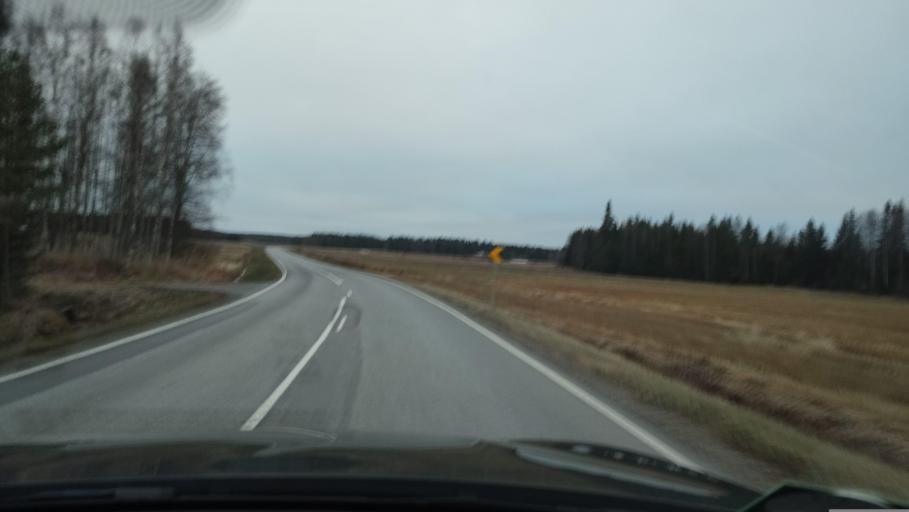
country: FI
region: Southern Ostrobothnia
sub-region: Suupohja
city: Karijoki
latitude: 62.3261
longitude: 21.8158
